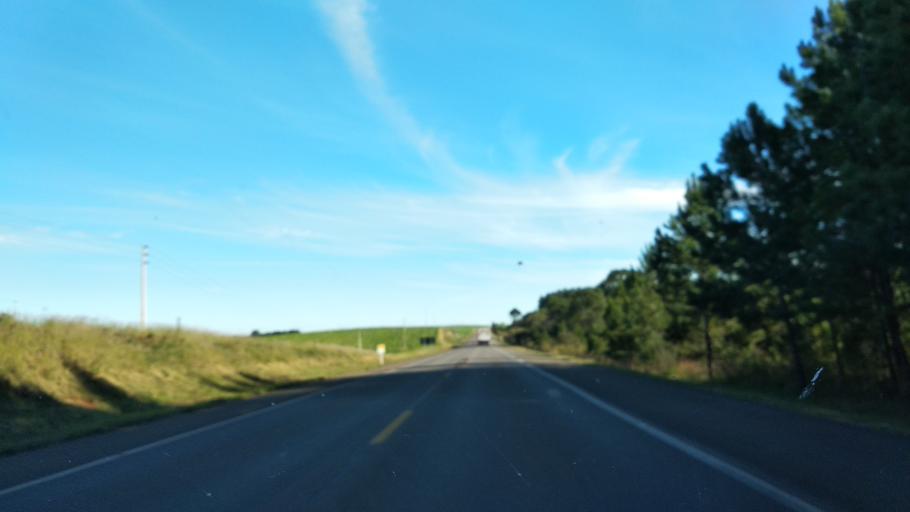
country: BR
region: Santa Catarina
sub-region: Celso Ramos
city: Celso Ramos
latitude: -27.5115
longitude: -51.3475
